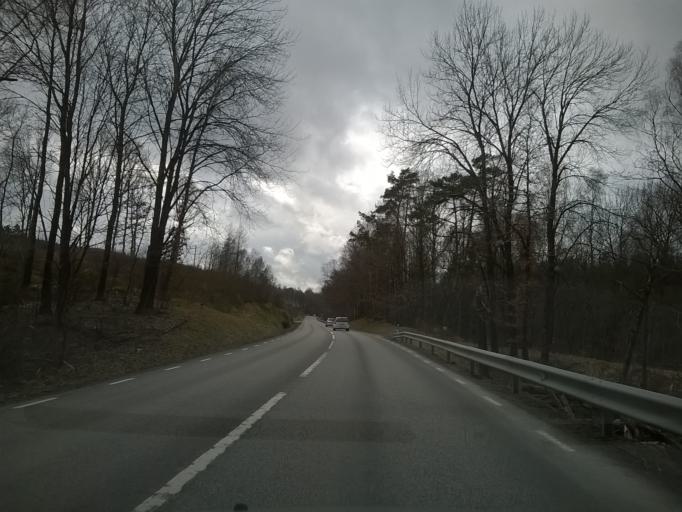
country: SE
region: Halland
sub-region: Varbergs Kommun
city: Tvaaker
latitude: 57.1455
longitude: 12.5020
